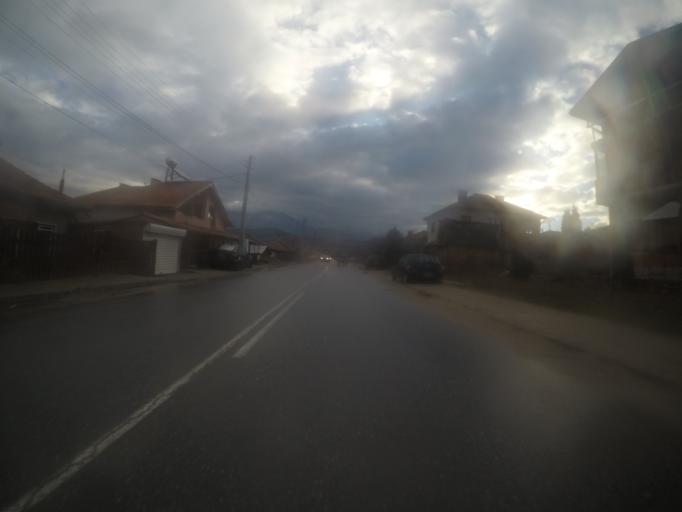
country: BG
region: Blagoevgrad
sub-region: Obshtina Simitli
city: Simitli
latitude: 41.8802
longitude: 23.1255
